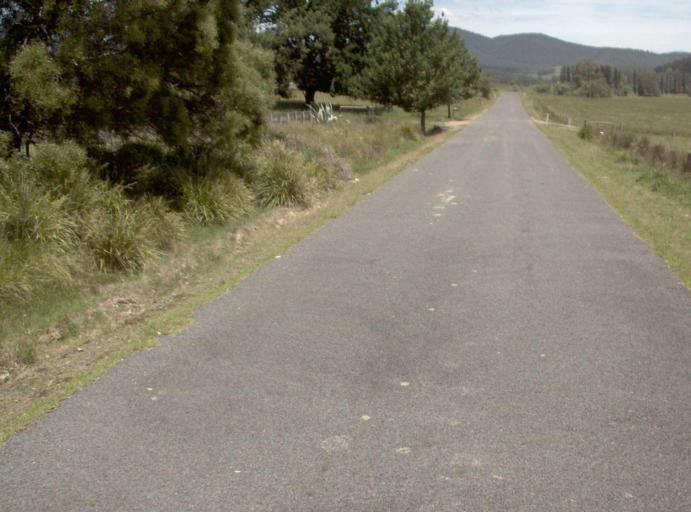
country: AU
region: New South Wales
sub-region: Bombala
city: Bombala
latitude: -37.4064
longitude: 149.0107
